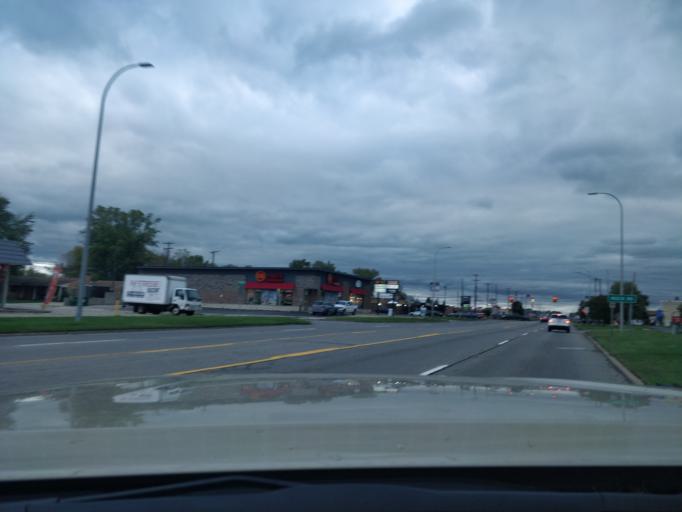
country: US
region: Michigan
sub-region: Wayne County
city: Southgate
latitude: 42.1987
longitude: -83.2208
